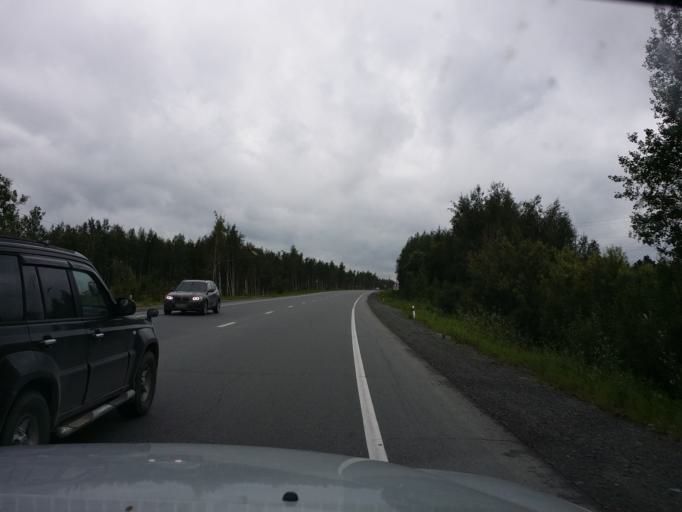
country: RU
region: Khanty-Mansiyskiy Avtonomnyy Okrug
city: Nizhnevartovsk
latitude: 61.0423
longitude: 76.3517
